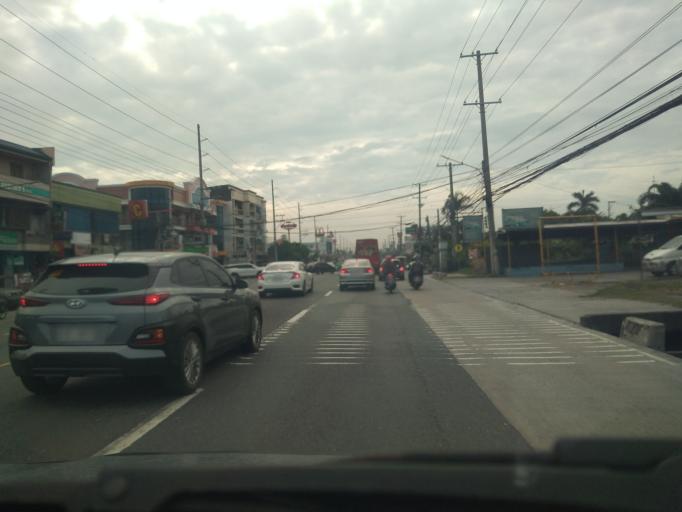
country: PH
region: Central Luzon
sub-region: Province of Pampanga
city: Bulaon
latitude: 15.0671
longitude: 120.6499
